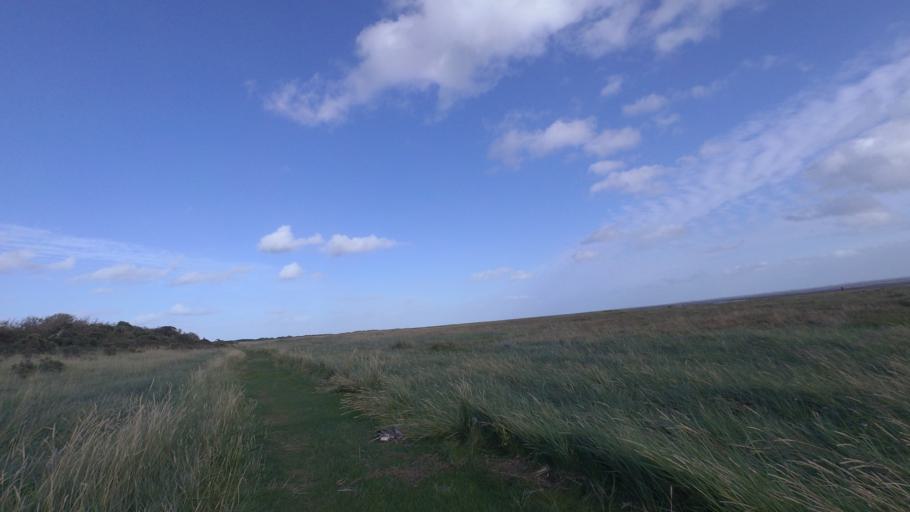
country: NL
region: Friesland
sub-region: Gemeente Dongeradeel
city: Ternaard
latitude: 53.4585
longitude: 5.9161
